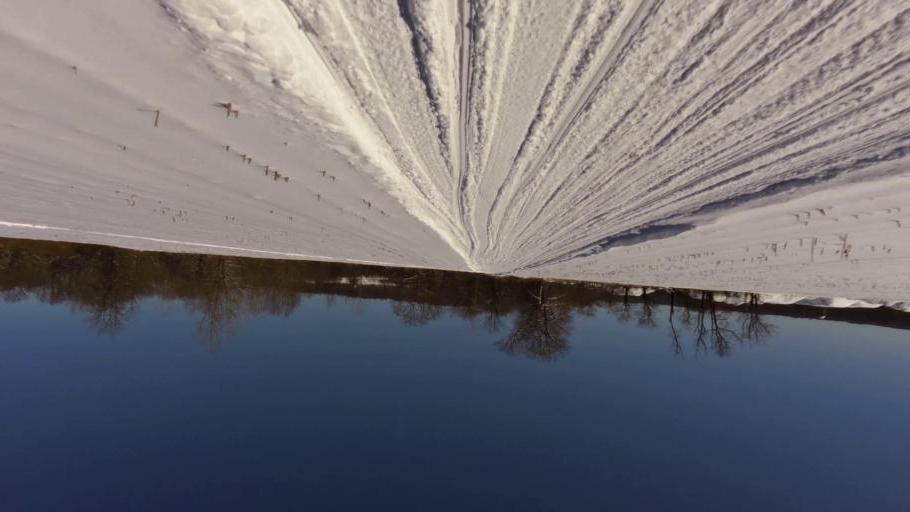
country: US
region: New York
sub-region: Chautauqua County
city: Celoron
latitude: 42.2492
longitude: -79.2717
